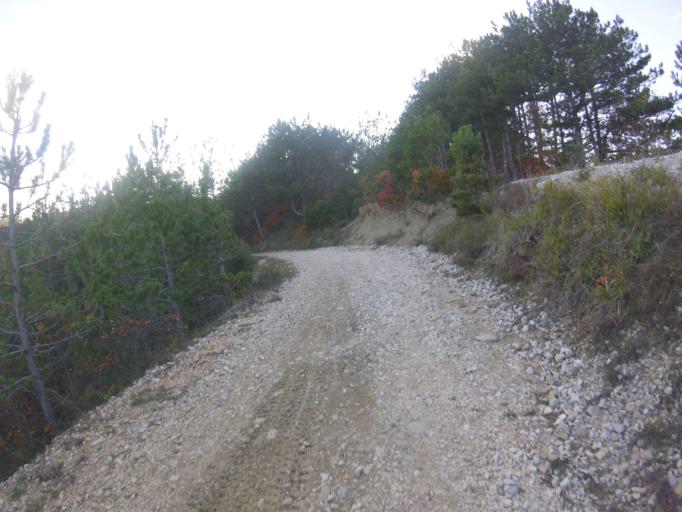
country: HR
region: Istarska
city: Pazin
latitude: 45.2273
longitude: 14.0053
